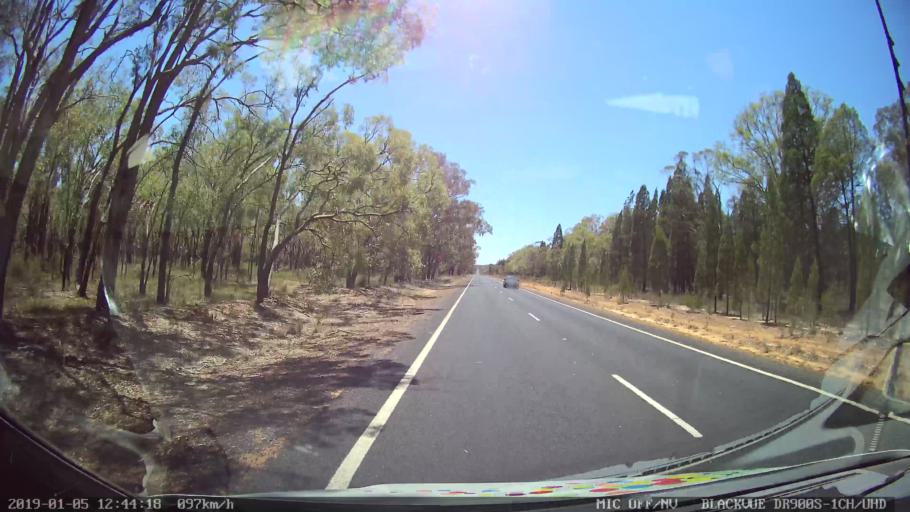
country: AU
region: New South Wales
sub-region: Warrumbungle Shire
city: Coonabarabran
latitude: -31.1391
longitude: 149.5356
